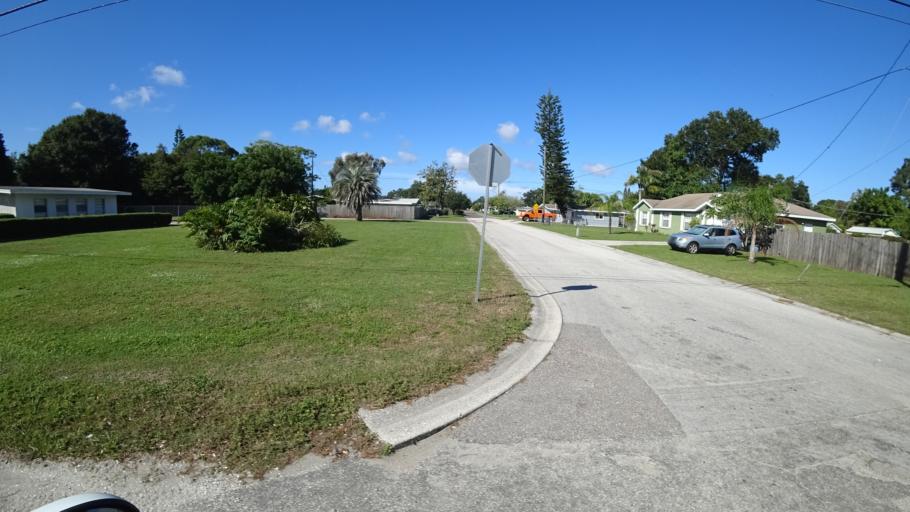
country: US
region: Florida
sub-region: Manatee County
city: South Bradenton
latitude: 27.4820
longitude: -82.5876
